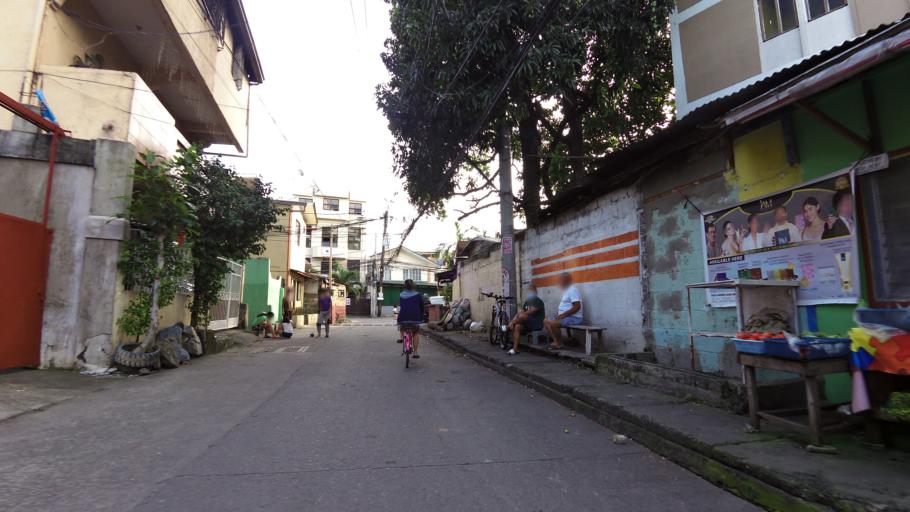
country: PH
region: Metro Manila
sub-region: Pasig
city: Pasig City
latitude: 14.5675
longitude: 121.0781
